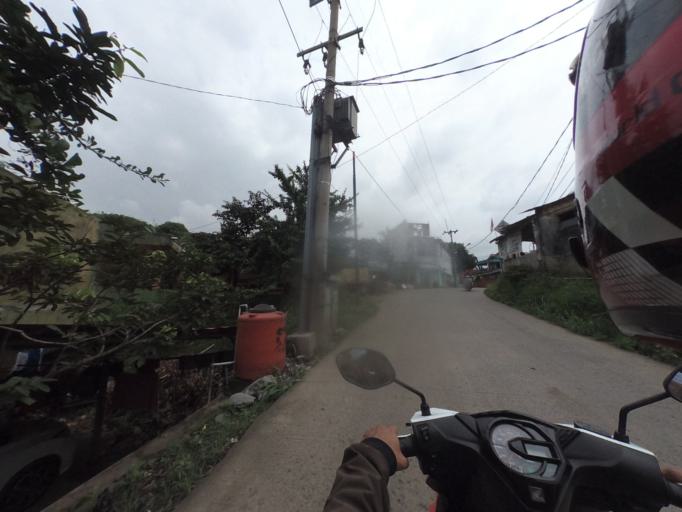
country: ID
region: West Java
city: Bogor
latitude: -6.6053
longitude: 106.7587
